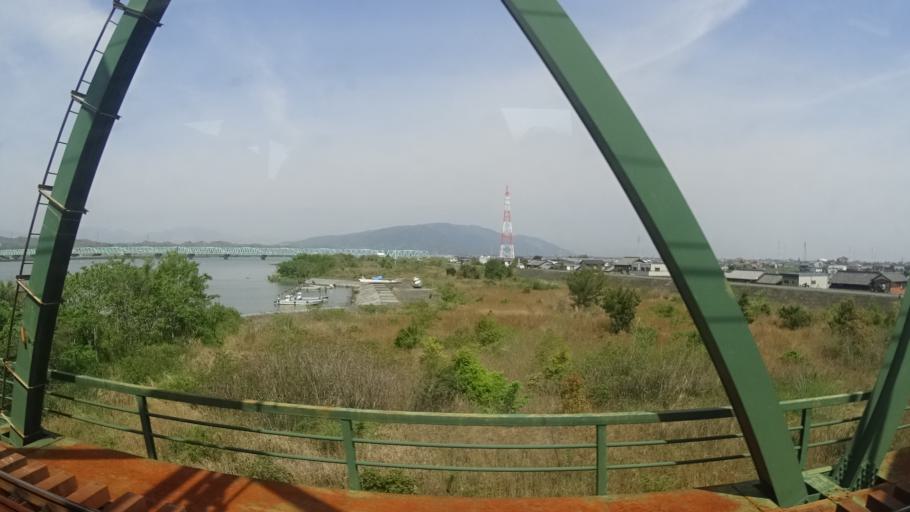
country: JP
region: Aichi
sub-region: Tsushima-shi
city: Tsushima
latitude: 35.0941
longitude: 136.6877
